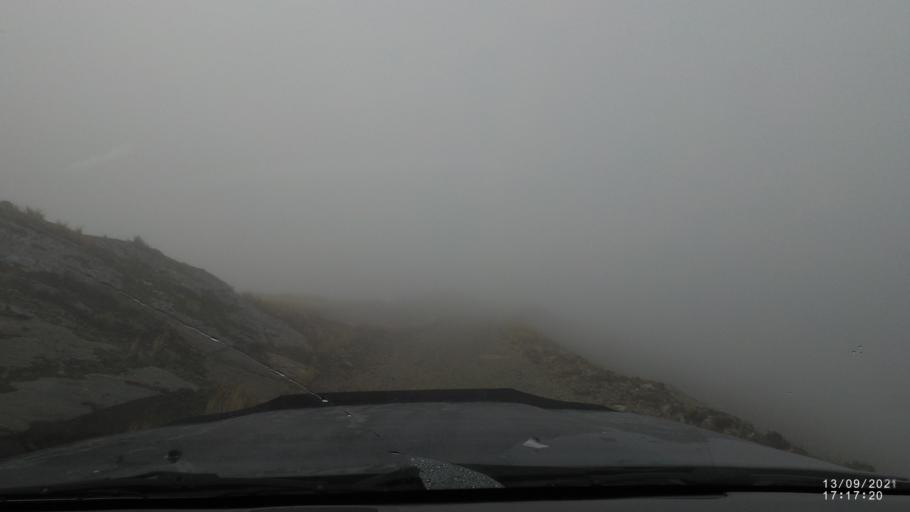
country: BO
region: Cochabamba
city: Colomi
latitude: -17.3453
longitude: -65.7602
